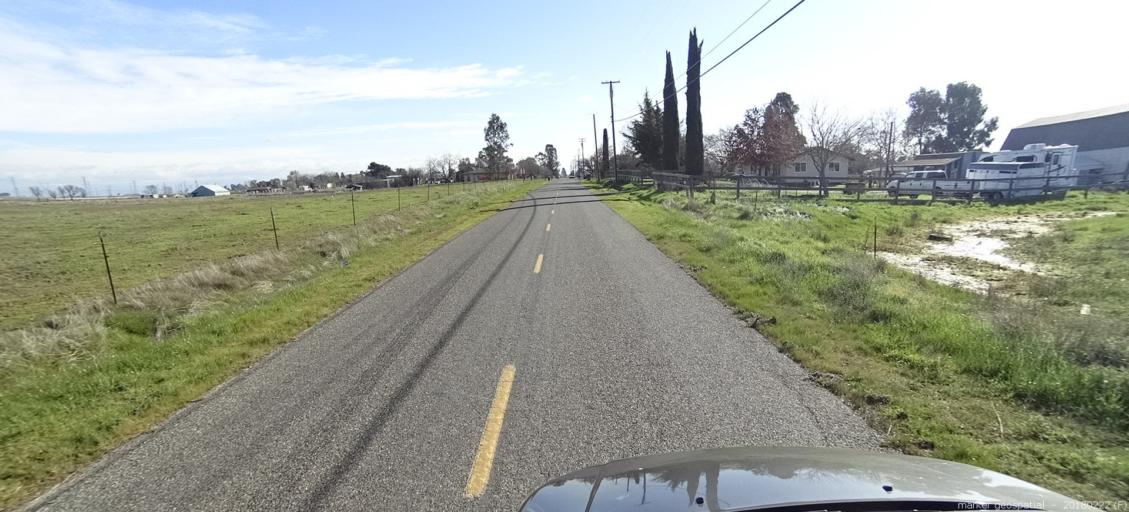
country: US
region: California
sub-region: Sacramento County
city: Elverta
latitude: 38.7322
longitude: -121.4627
